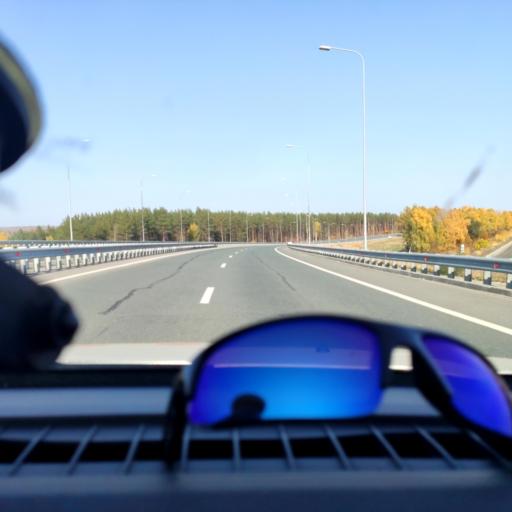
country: RU
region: Samara
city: Bereza
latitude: 53.5027
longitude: 50.1180
